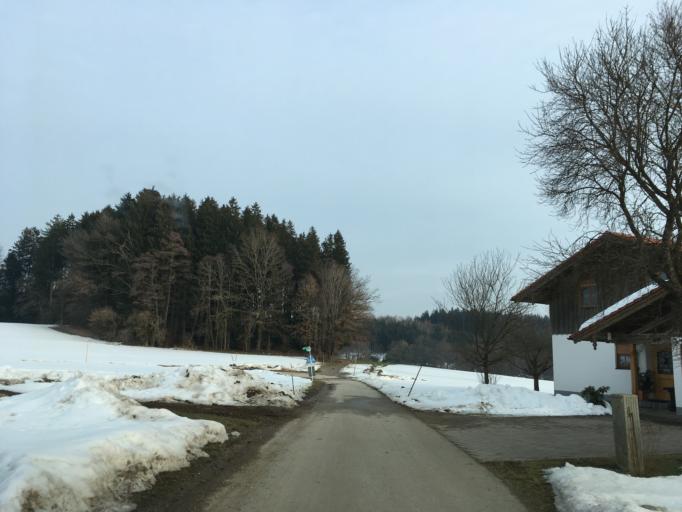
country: DE
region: Bavaria
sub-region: Upper Bavaria
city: Bad Endorf
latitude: 47.9254
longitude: 12.2999
